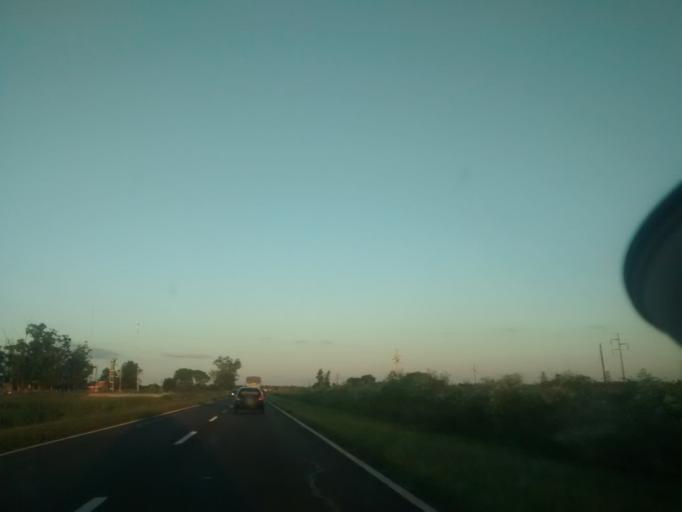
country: AR
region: Chaco
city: La Escondida
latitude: -27.1339
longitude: -59.4751
